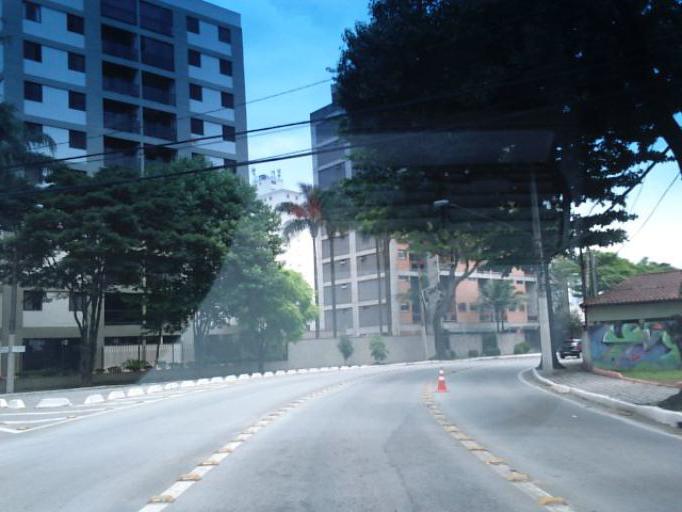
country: BR
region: Sao Paulo
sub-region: Sao Jose Dos Campos
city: Sao Jose dos Campos
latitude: -23.1898
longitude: -45.8898
